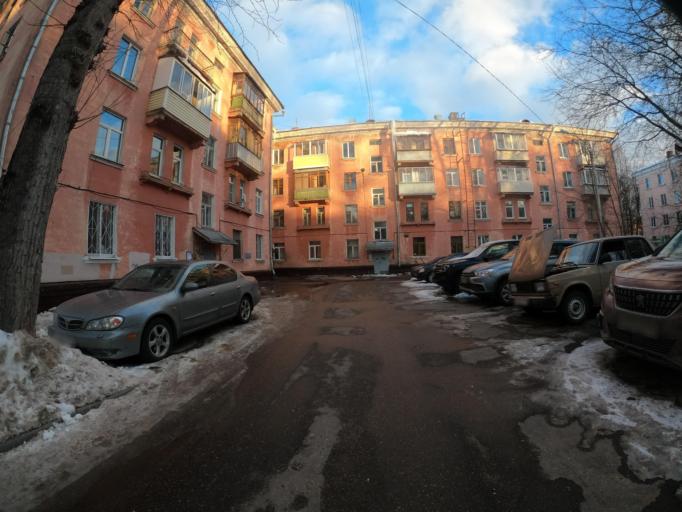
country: RU
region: Moskovskaya
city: Klimovsk
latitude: 55.3809
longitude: 37.5451
